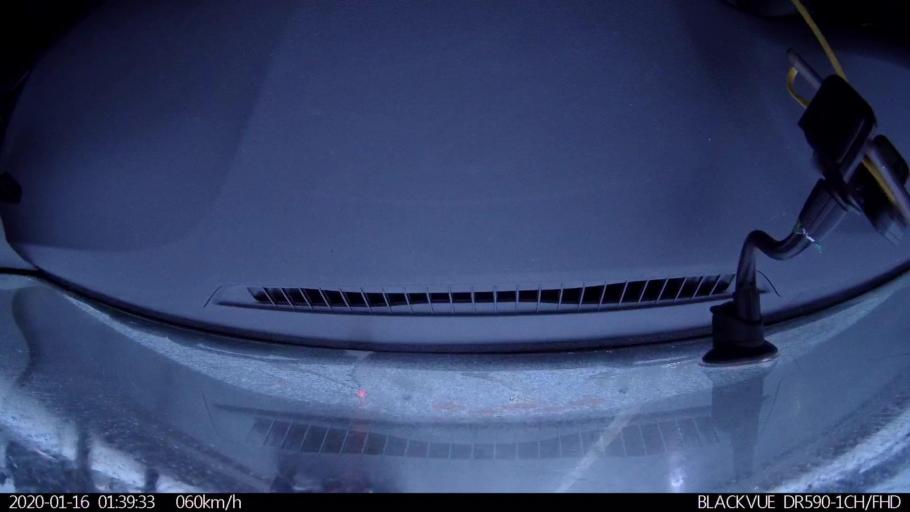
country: RU
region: Nizjnij Novgorod
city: Gorbatovka
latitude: 56.3337
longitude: 43.7940
